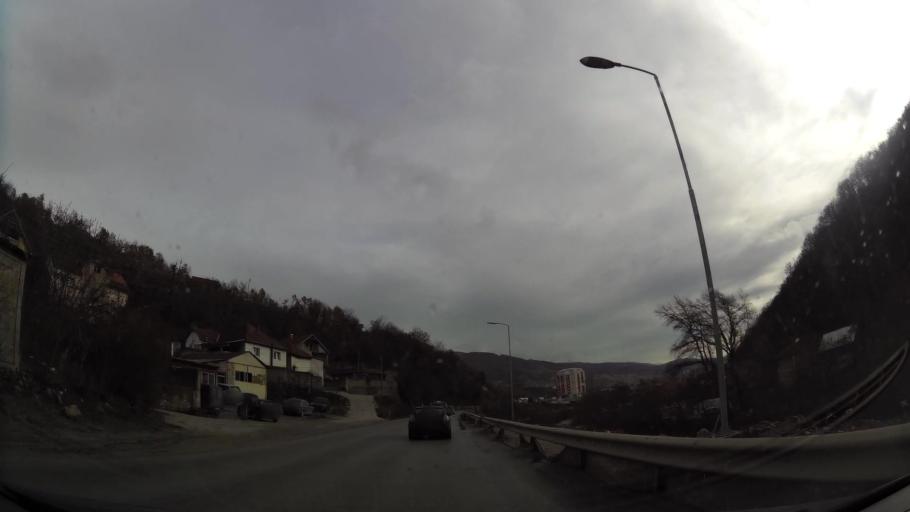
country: XK
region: Ferizaj
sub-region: Hani i Elezit
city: Hani i Elezit
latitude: 42.1577
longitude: 21.2900
